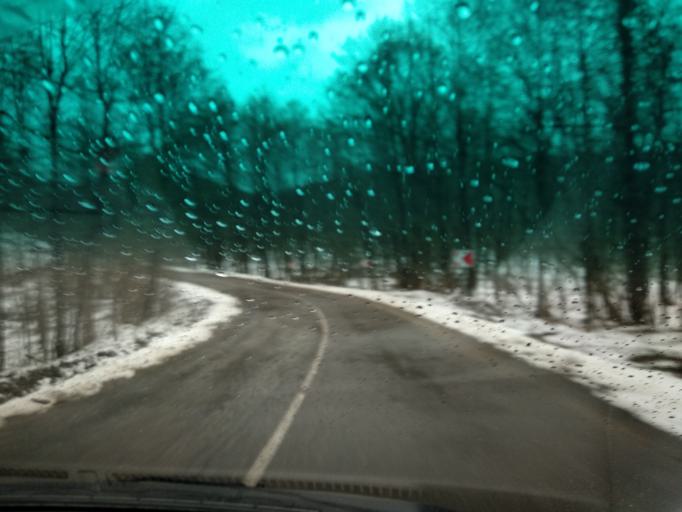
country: RU
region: Krasnodarskiy
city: Khadyzhensk
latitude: 44.2185
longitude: 39.3996
